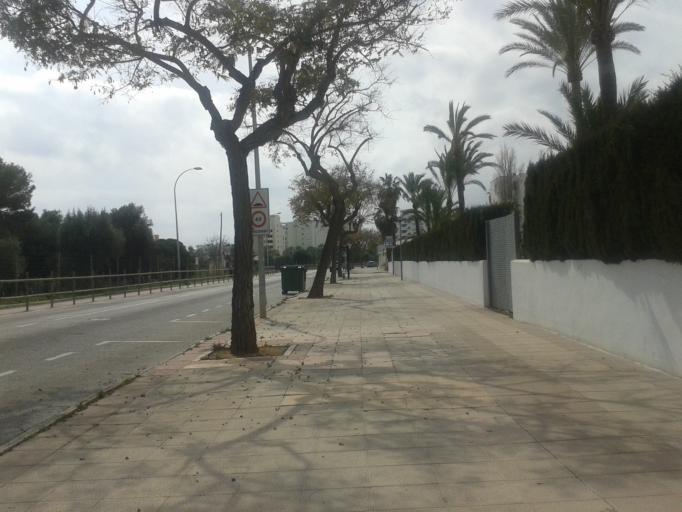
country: ES
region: Balearic Islands
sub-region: Illes Balears
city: Son Servera
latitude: 39.5803
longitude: 3.3790
